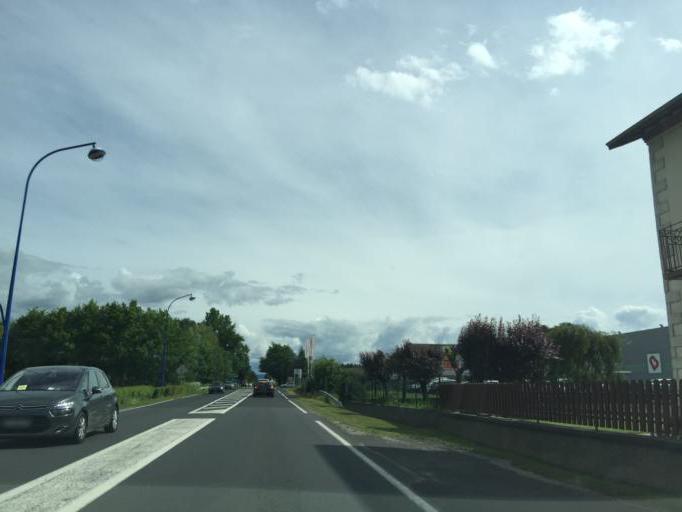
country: FR
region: Auvergne
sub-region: Departement du Puy-de-Dome
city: Ambert
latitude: 45.5418
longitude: 3.7282
